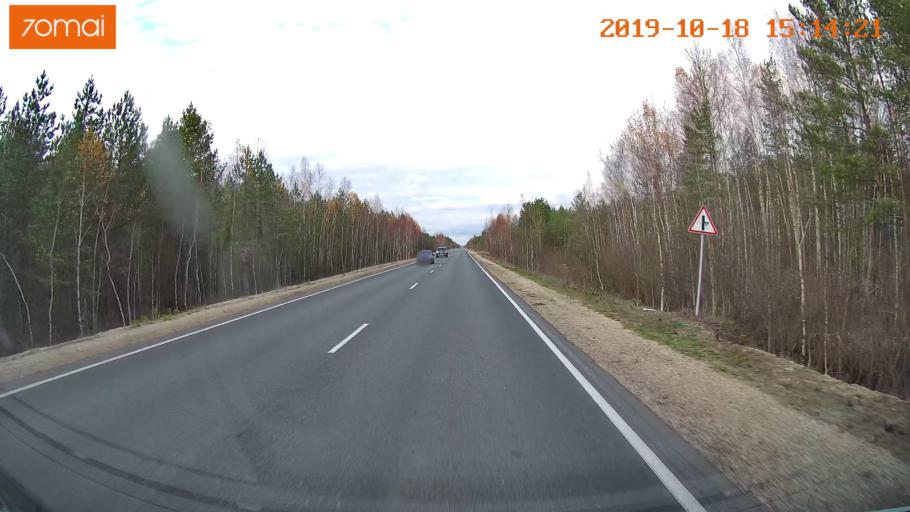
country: RU
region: Vladimir
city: Gus'-Khrustal'nyy
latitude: 55.6013
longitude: 40.7201
